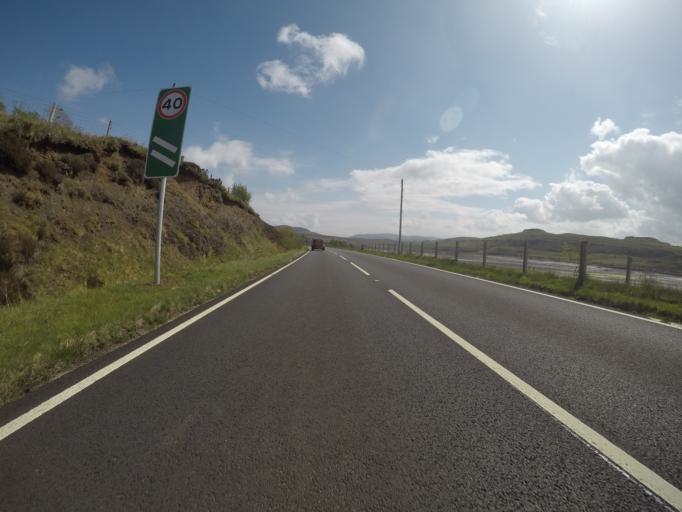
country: GB
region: Scotland
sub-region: Highland
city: Portree
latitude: 57.4904
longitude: -6.3163
